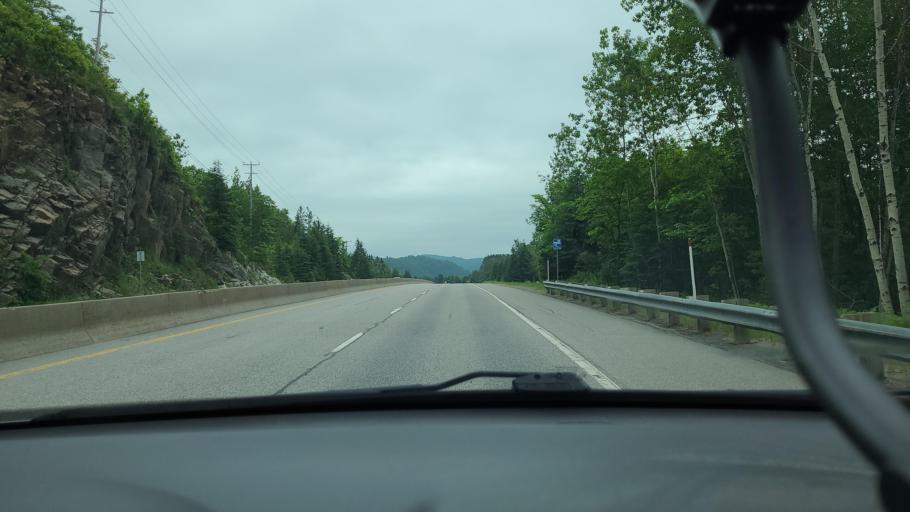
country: CA
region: Quebec
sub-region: Laurentides
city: Labelle
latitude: 46.1991
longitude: -74.7234
